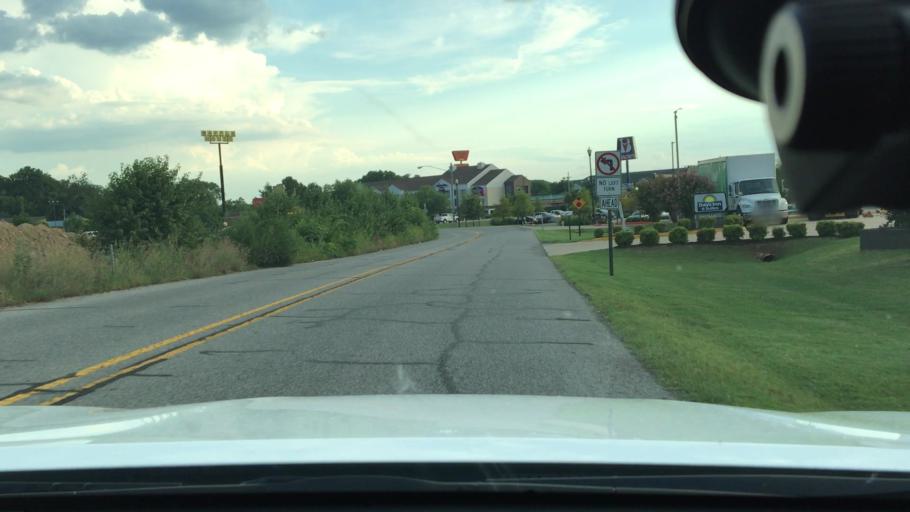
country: US
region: Arkansas
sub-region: Benton County
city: Bentonville
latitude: 36.3361
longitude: -94.1845
